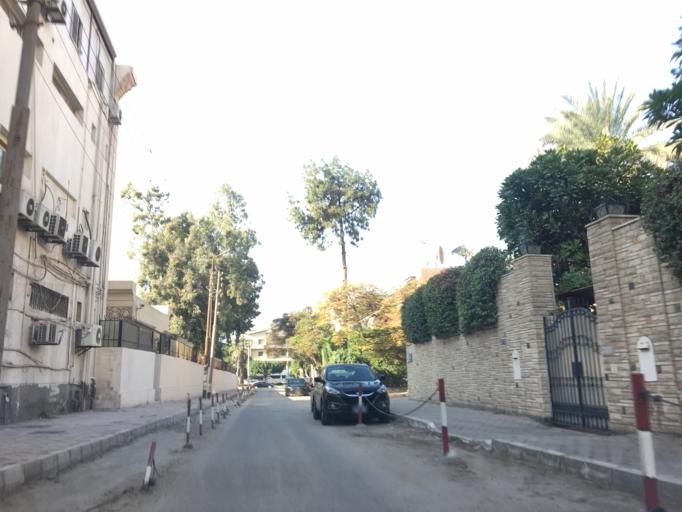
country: EG
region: Muhafazat al Qahirah
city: Cairo
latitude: 30.0863
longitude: 31.3286
